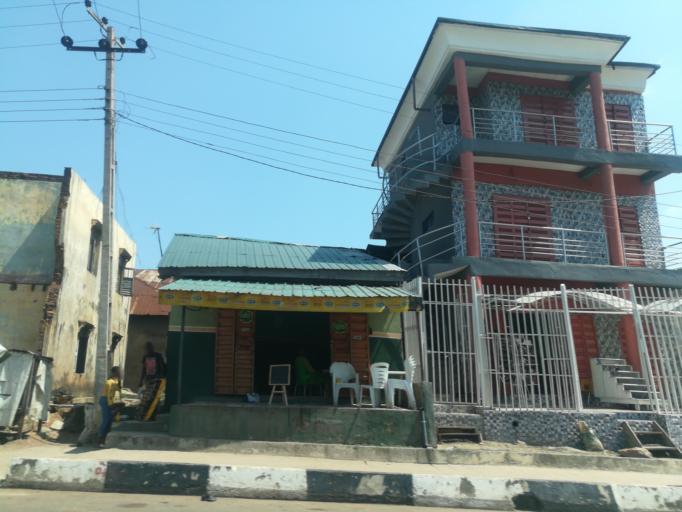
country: NG
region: Ogun
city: Abeokuta
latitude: 7.1614
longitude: 3.3501
